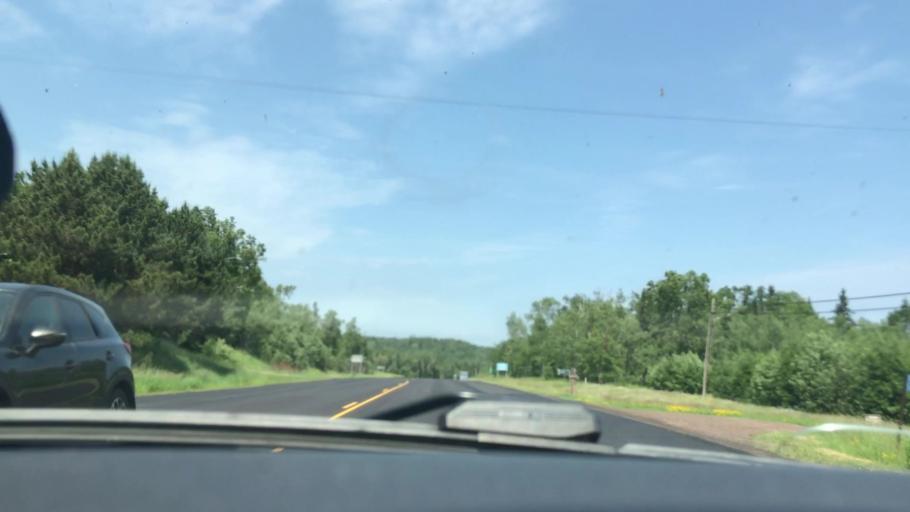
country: US
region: Minnesota
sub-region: Lake County
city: Silver Bay
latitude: 47.3320
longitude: -91.2065
